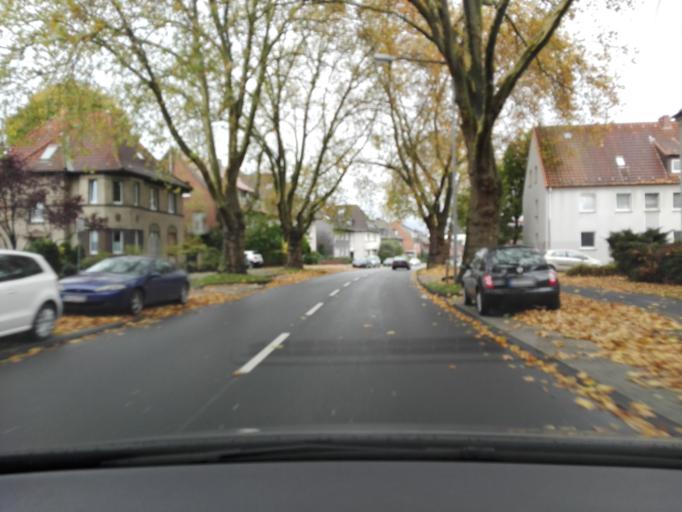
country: DE
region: North Rhine-Westphalia
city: Lunen
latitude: 51.6215
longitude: 7.5164
